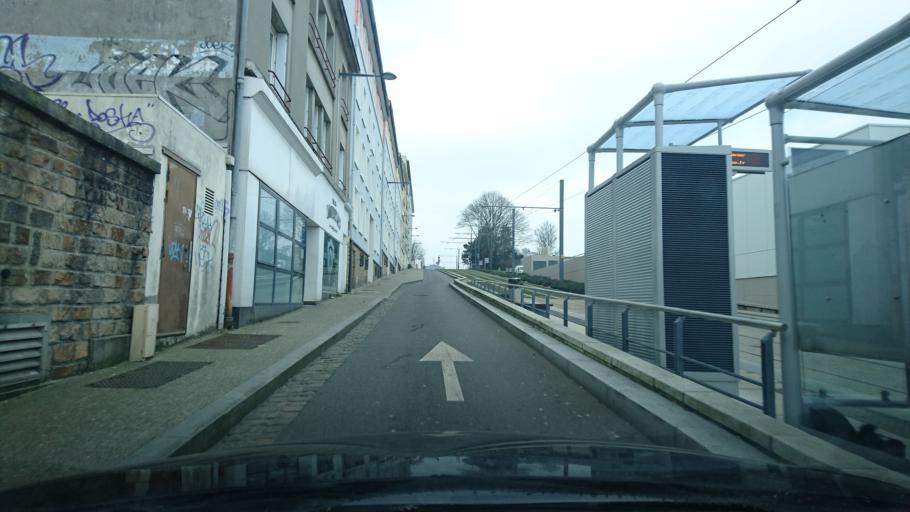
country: FR
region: Brittany
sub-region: Departement du Finistere
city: Brest
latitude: 48.3847
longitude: -4.5040
